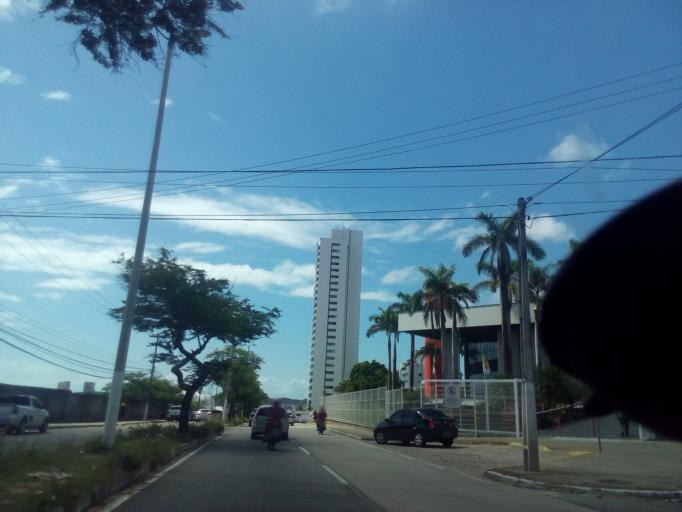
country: BR
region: Rio Grande do Norte
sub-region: Natal
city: Natal
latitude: -5.8248
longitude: -35.2238
